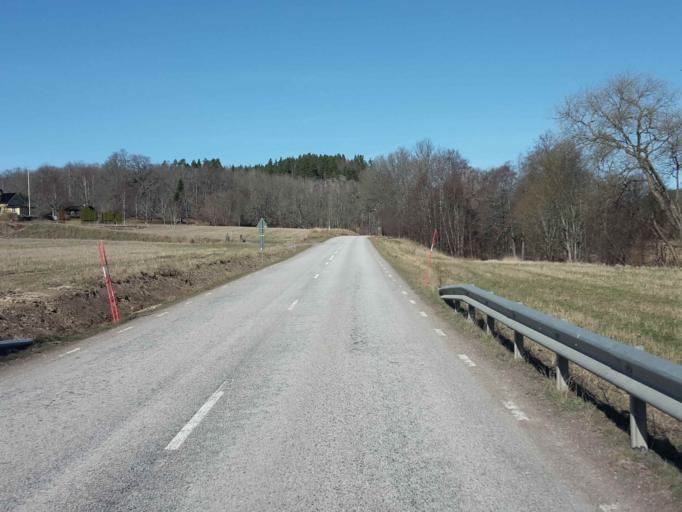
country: SE
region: Kalmar
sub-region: Vasterviks Kommun
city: Overum
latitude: 58.1364
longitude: 16.2190
